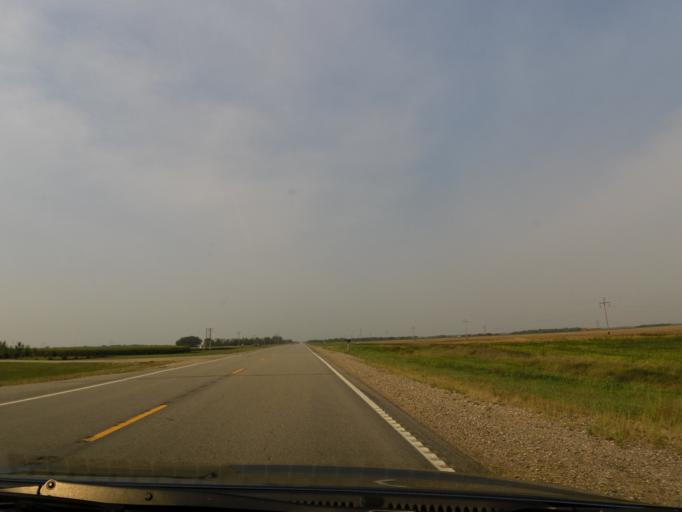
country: US
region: North Dakota
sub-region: Cass County
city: Horace
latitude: 46.6303
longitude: -96.8512
